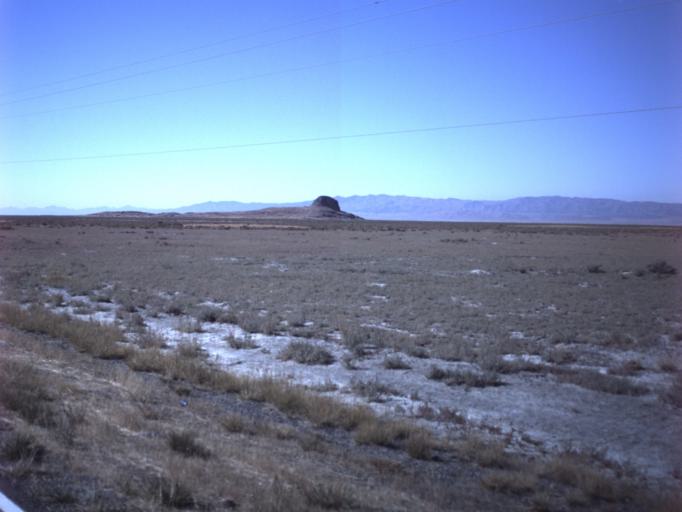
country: US
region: Utah
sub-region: Tooele County
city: Grantsville
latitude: 40.7267
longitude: -112.6585
